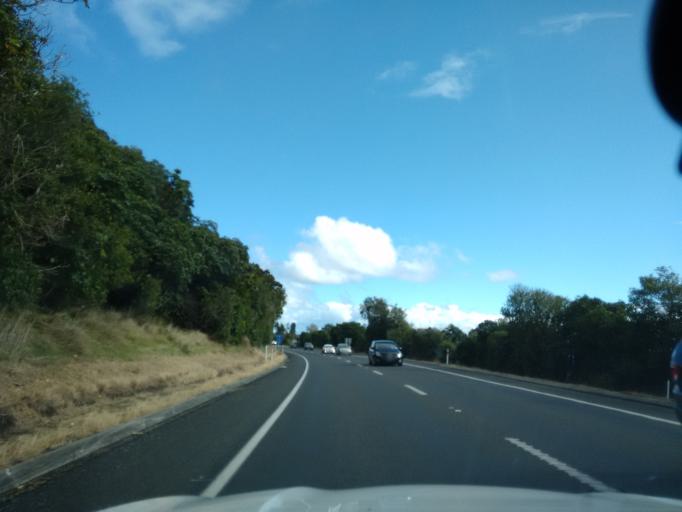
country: NZ
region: Waikato
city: Turangi
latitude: -38.8882
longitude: 175.9523
